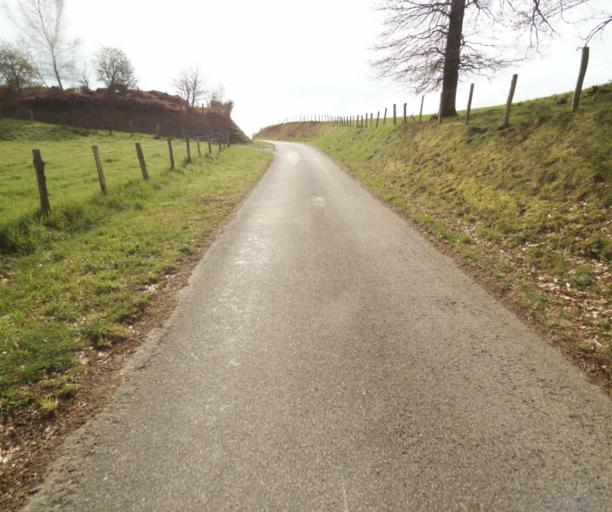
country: FR
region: Limousin
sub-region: Departement de la Correze
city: Correze
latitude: 45.3528
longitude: 1.8667
